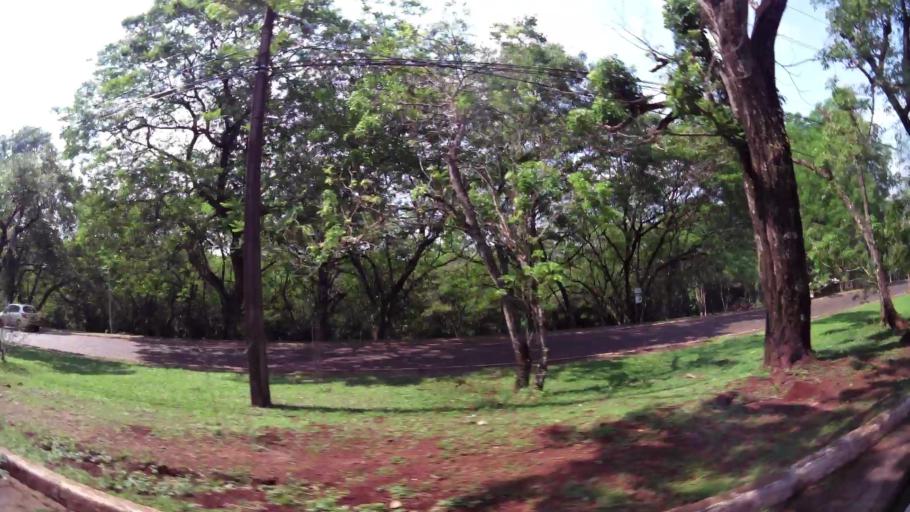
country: PY
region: Alto Parana
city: Ciudad del Este
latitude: -25.5173
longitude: -54.6249
